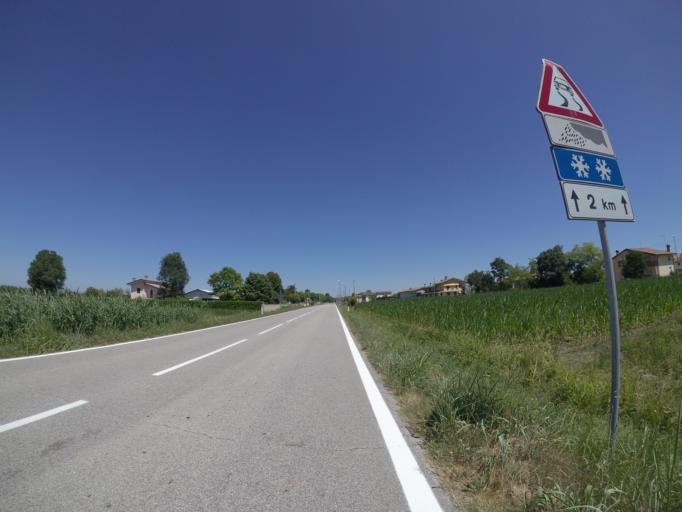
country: IT
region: Friuli Venezia Giulia
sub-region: Provincia di Udine
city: Teor
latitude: 45.8487
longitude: 13.0292
